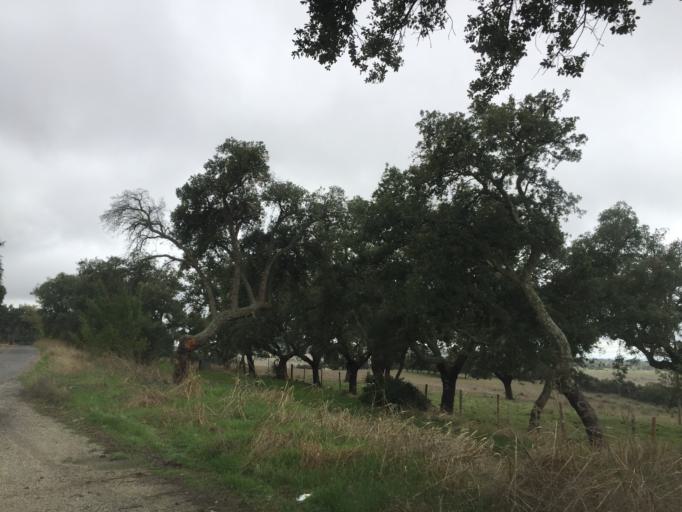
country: PT
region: Portalegre
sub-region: Alter do Chao
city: Alter do Chao
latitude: 39.2378
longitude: -7.6530
